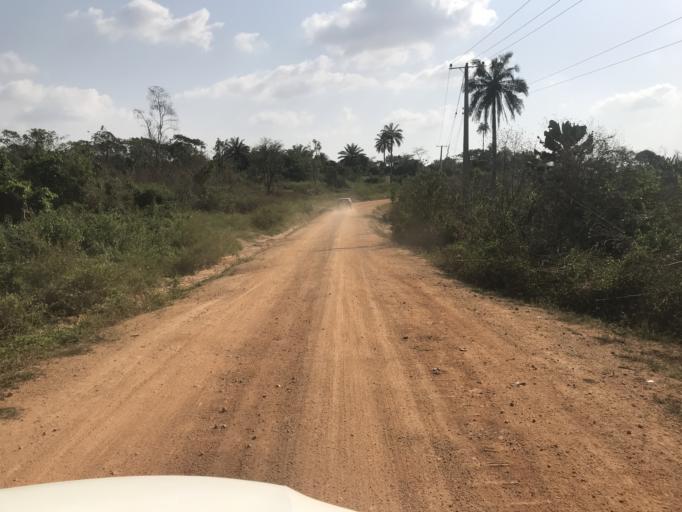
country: NG
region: Osun
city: Osogbo
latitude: 7.8521
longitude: 4.5856
